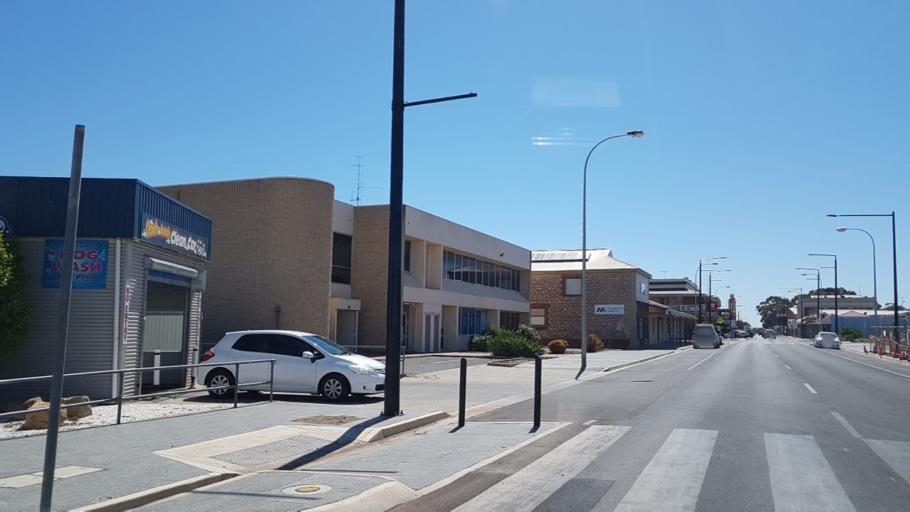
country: AU
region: South Australia
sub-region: Copper Coast
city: Kadina
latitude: -33.9631
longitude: 137.7104
